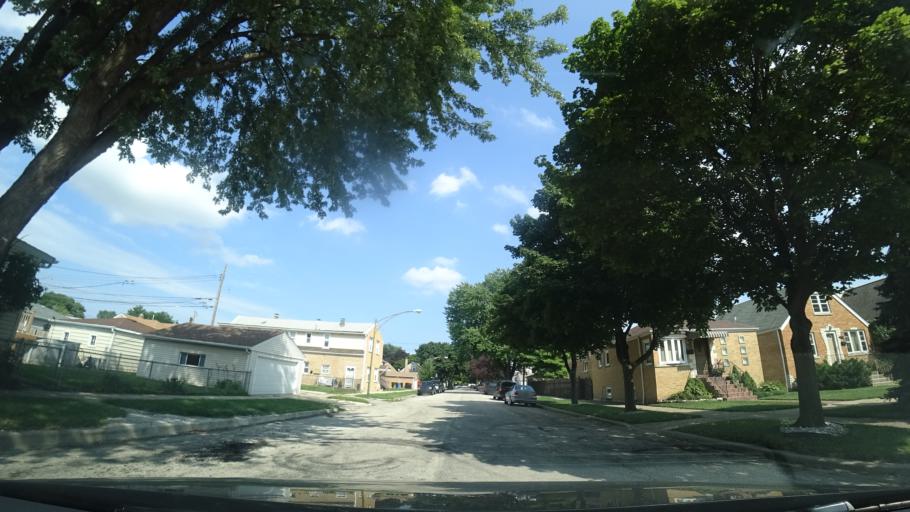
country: US
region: Illinois
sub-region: Cook County
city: Harwood Heights
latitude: 41.9792
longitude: -87.7851
